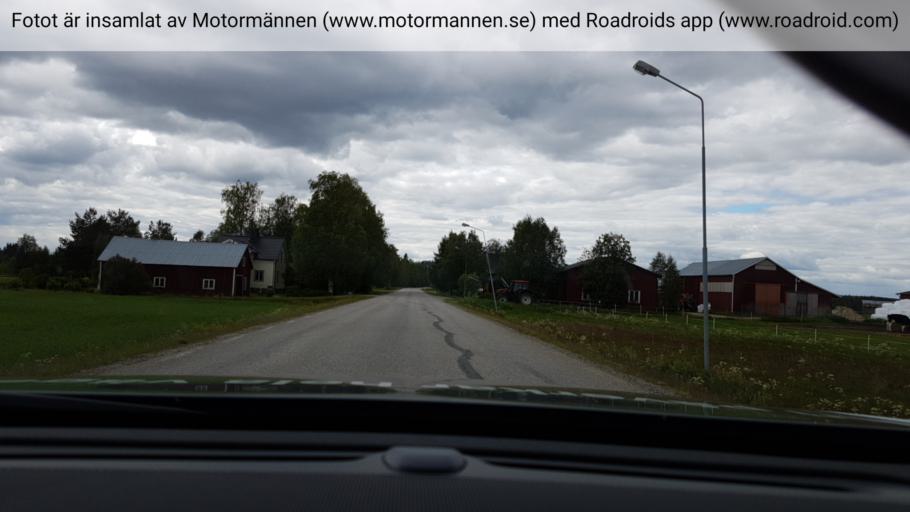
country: SE
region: Vaesterbotten
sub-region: Vindelns Kommun
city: Vindeln
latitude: 64.0883
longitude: 19.6491
